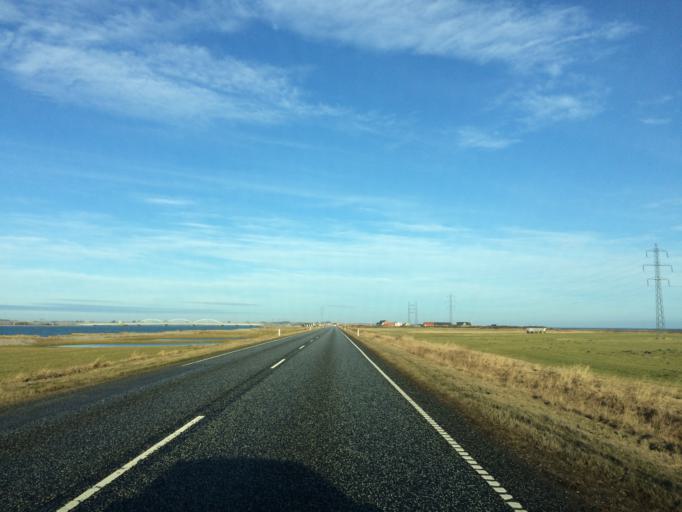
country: DK
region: Central Jutland
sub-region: Struer Kommune
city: Struer
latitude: 56.5649
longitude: 8.5592
